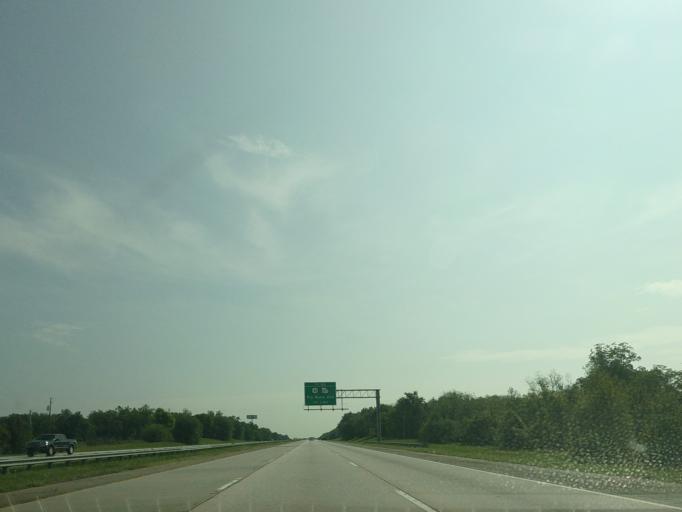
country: US
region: Georgia
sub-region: Bibb County
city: Macon
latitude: 32.7770
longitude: -83.6848
